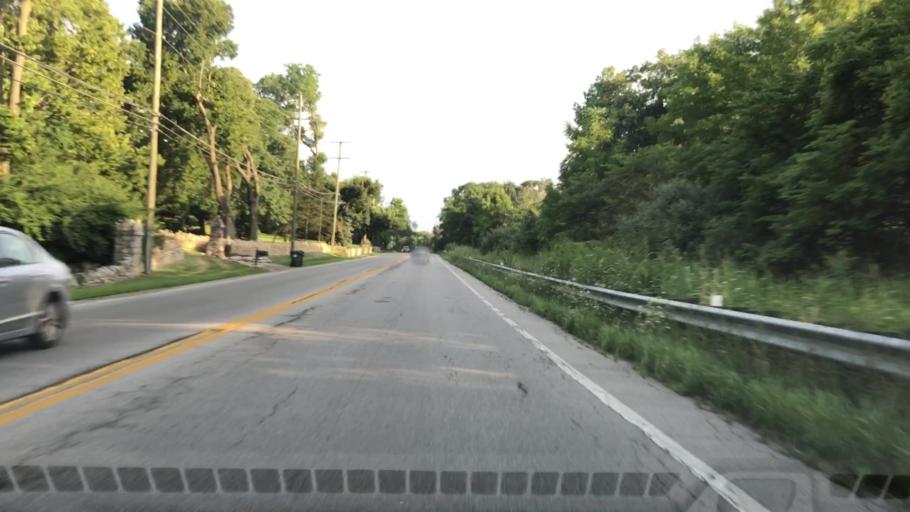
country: US
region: Ohio
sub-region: Franklin County
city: Dublin
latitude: 40.0788
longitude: -83.1094
